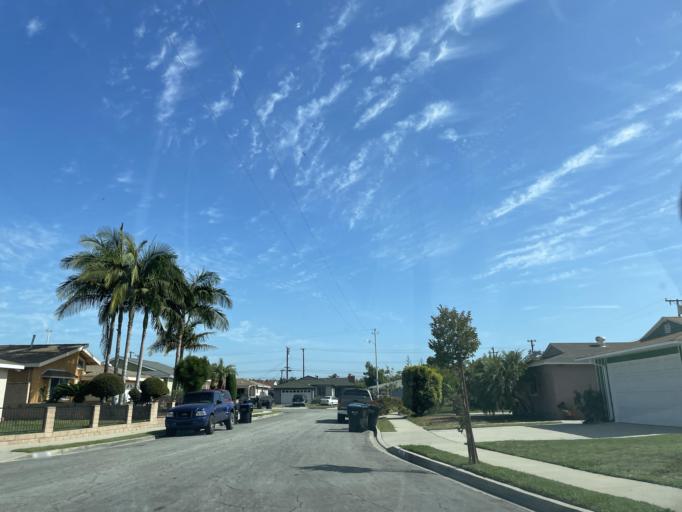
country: US
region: California
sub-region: Los Angeles County
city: Norwalk
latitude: 33.9110
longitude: -118.0621
